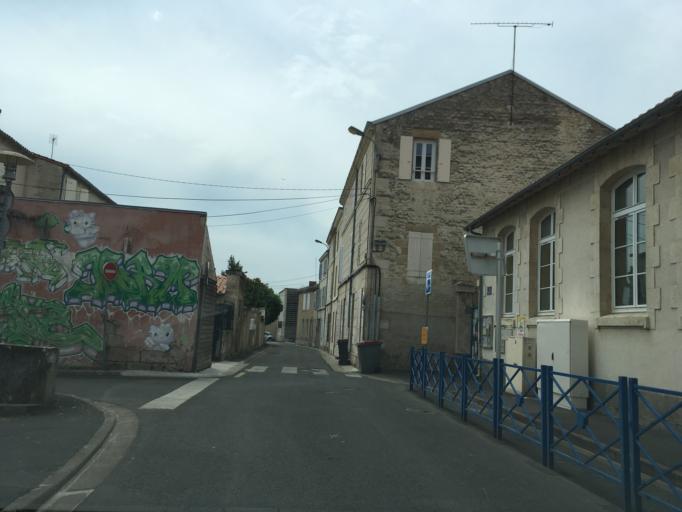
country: FR
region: Poitou-Charentes
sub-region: Departement des Deux-Sevres
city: Niort
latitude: 46.3190
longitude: -0.4586
